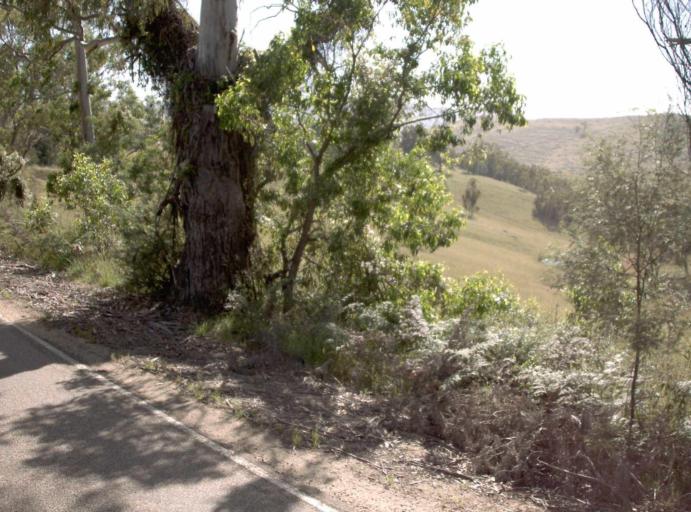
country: AU
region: Victoria
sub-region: East Gippsland
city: Lakes Entrance
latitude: -37.5174
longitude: 148.1625
